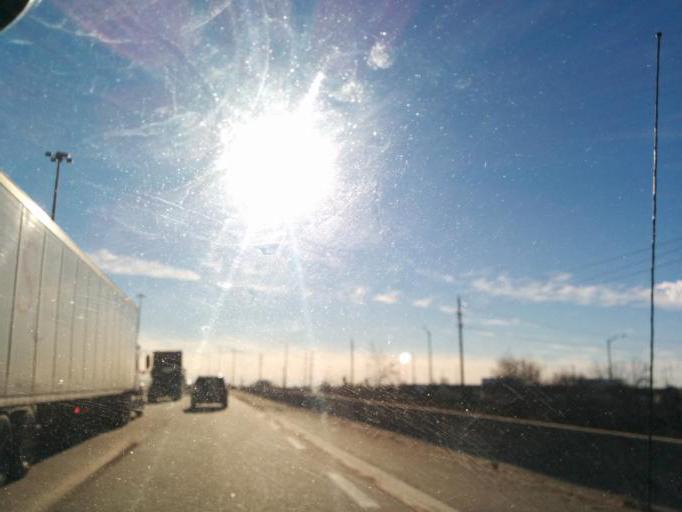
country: CA
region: Ontario
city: Etobicoke
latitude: 43.6892
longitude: -79.6030
